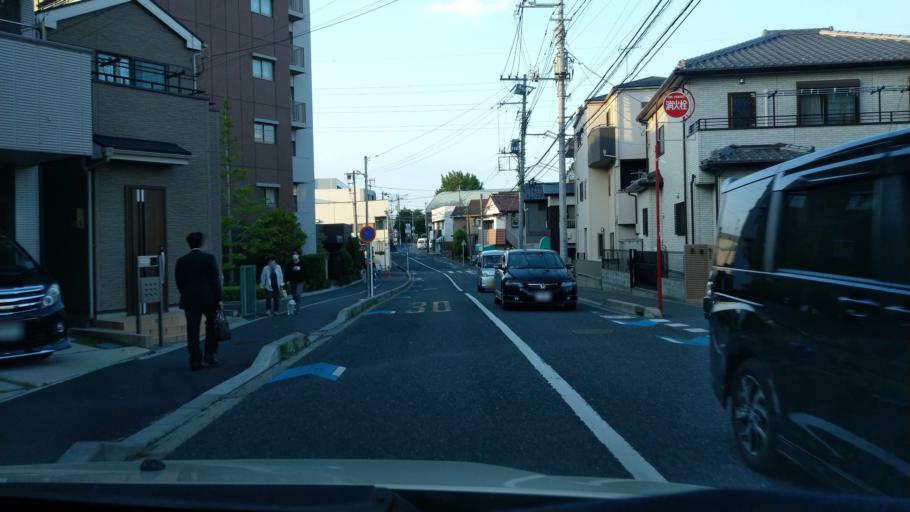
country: JP
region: Saitama
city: Yono
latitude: 35.8766
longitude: 139.6497
